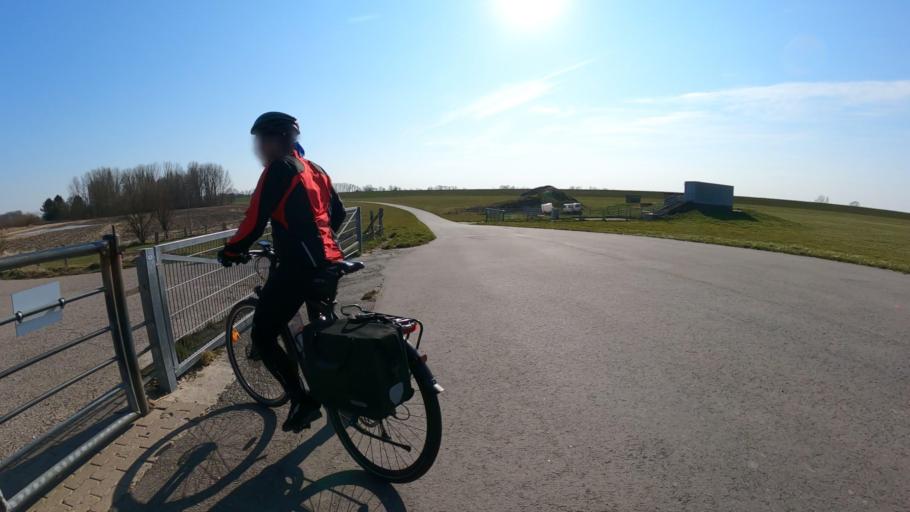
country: DE
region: Schleswig-Holstein
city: Seestermuhe
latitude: 53.7146
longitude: 9.5267
